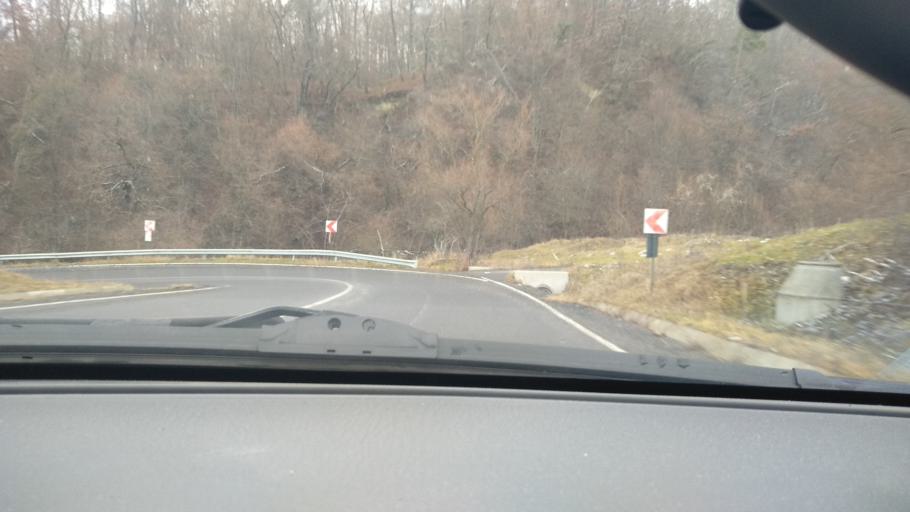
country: RO
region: Mures
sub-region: Comuna Magherani
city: Magherani
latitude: 46.5815
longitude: 24.9464
